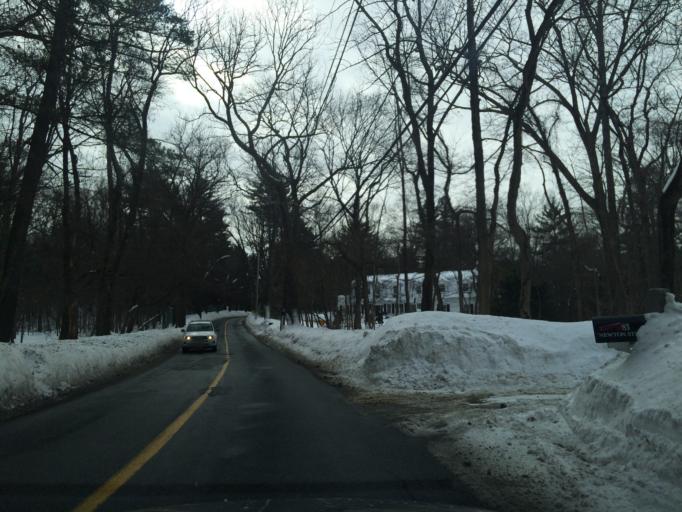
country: US
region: Massachusetts
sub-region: Middlesex County
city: Weston
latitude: 42.3500
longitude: -71.2830
